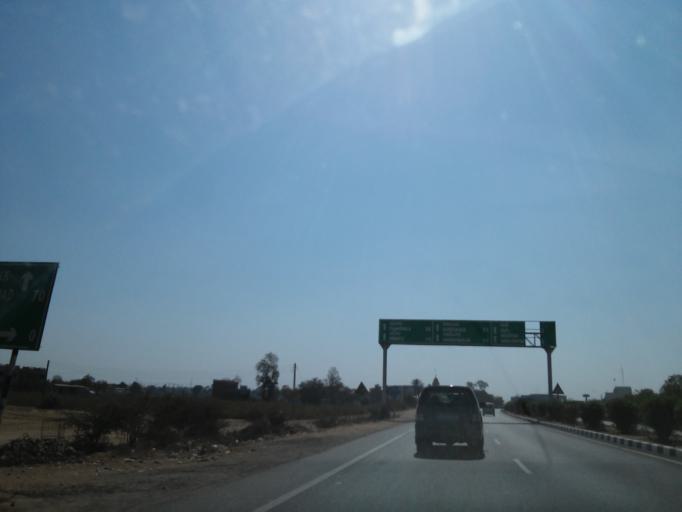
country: IN
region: Gujarat
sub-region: Sabar Kantha
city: Himatnagar
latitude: 23.5433
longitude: 72.9509
